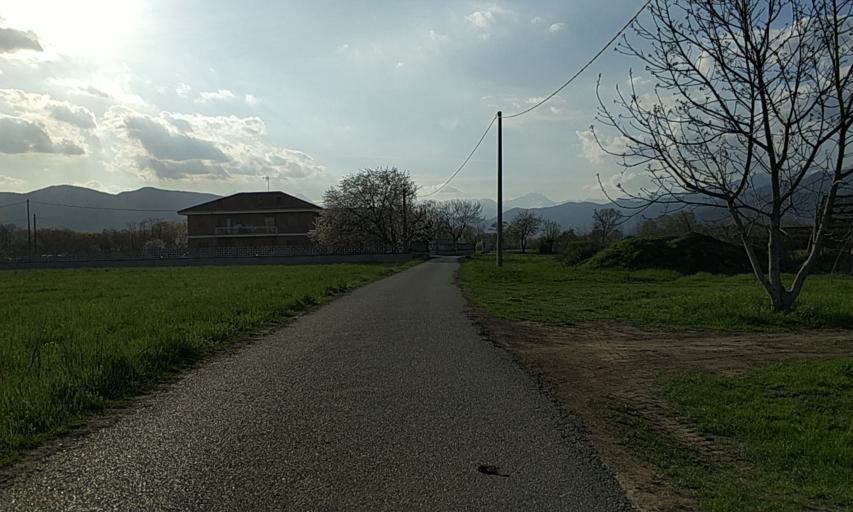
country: IT
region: Piedmont
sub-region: Provincia di Torino
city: San Carlo Canavese
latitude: 45.2422
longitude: 7.5933
